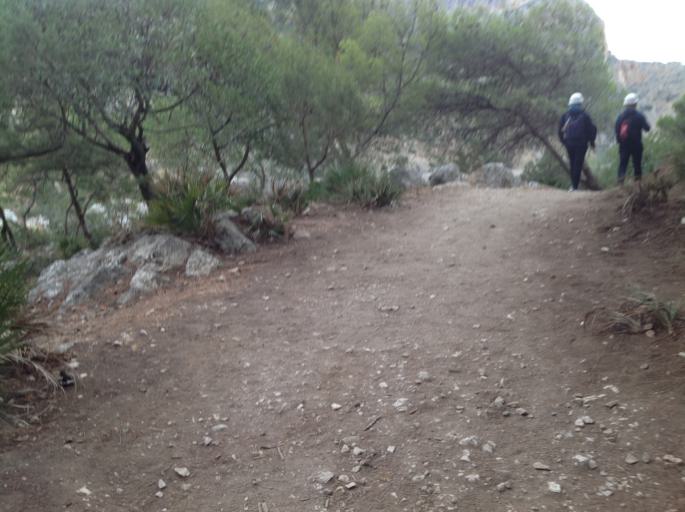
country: ES
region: Andalusia
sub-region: Provincia de Malaga
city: Ardales
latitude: 36.9223
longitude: -4.7808
